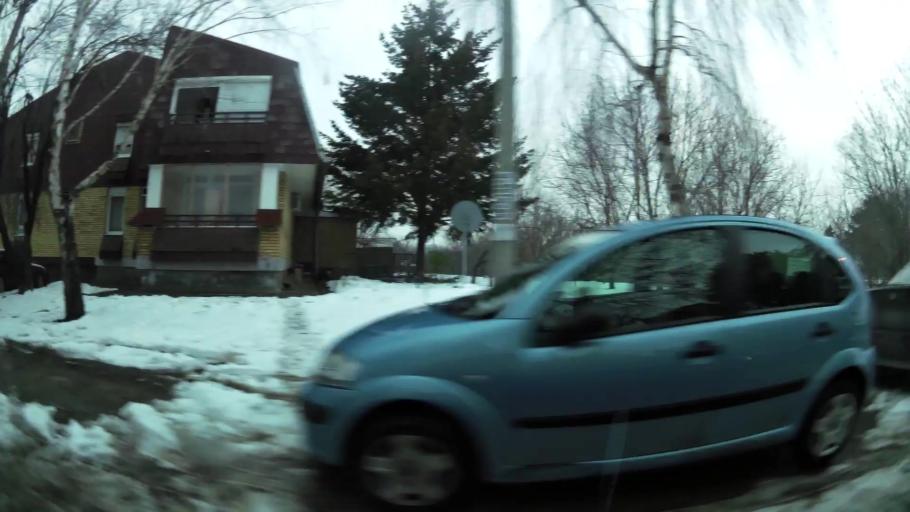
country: RS
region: Central Serbia
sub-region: Belgrade
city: Zemun
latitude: 44.8108
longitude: 20.3731
